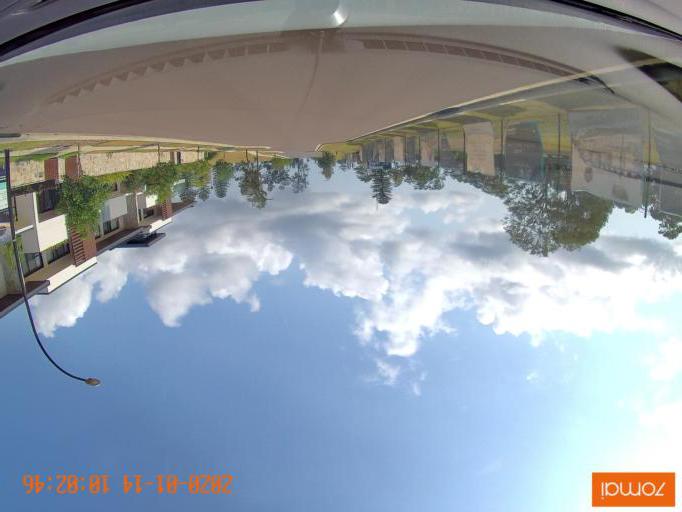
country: AU
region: New South Wales
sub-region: Wyong Shire
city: Kingfisher Shores
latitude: -33.1241
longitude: 151.5405
